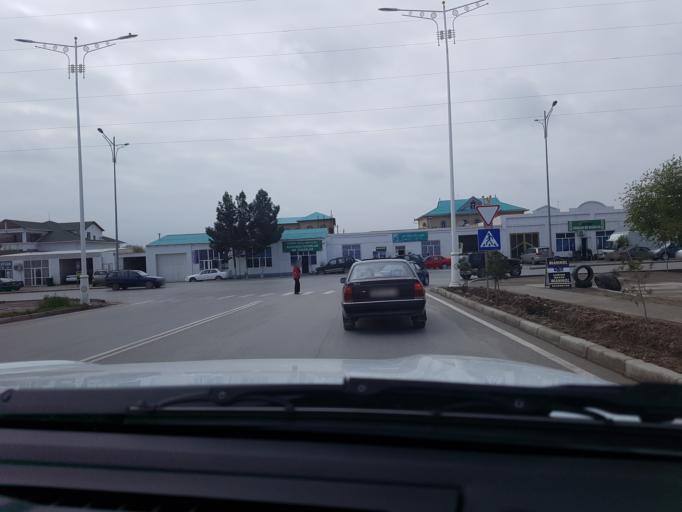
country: TM
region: Lebap
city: Turkmenabat
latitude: 39.0730
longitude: 63.5950
